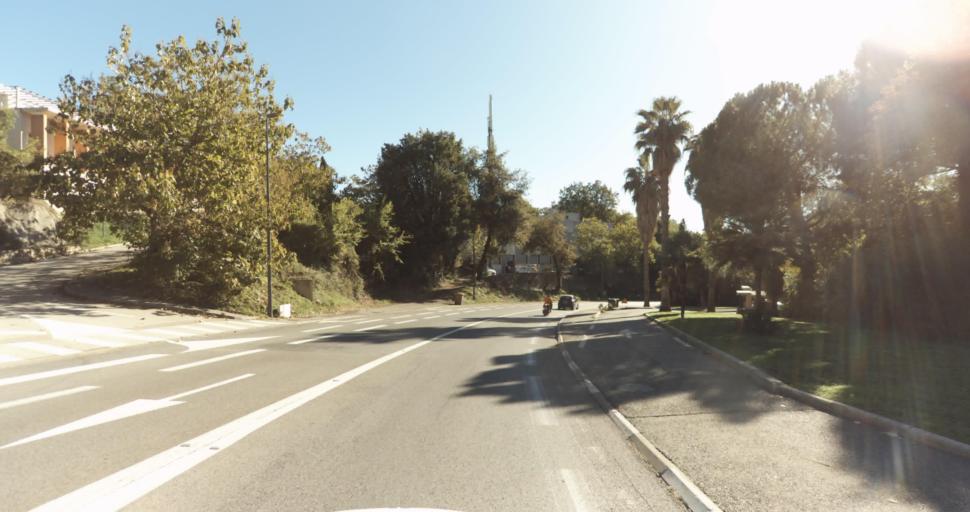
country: FR
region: Provence-Alpes-Cote d'Azur
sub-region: Departement des Alpes-Maritimes
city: Vence
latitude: 43.7194
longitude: 7.1132
